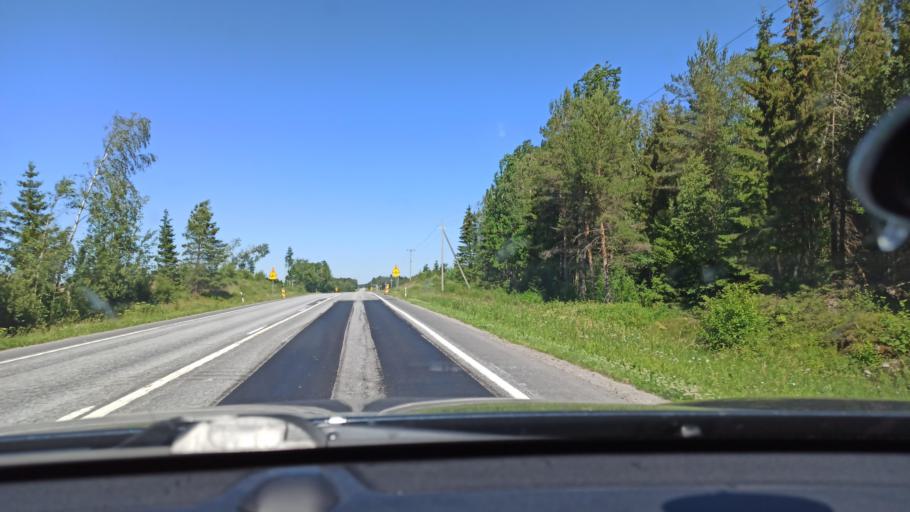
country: FI
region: Ostrobothnia
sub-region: Vaasa
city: Voera
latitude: 63.2339
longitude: 22.2494
